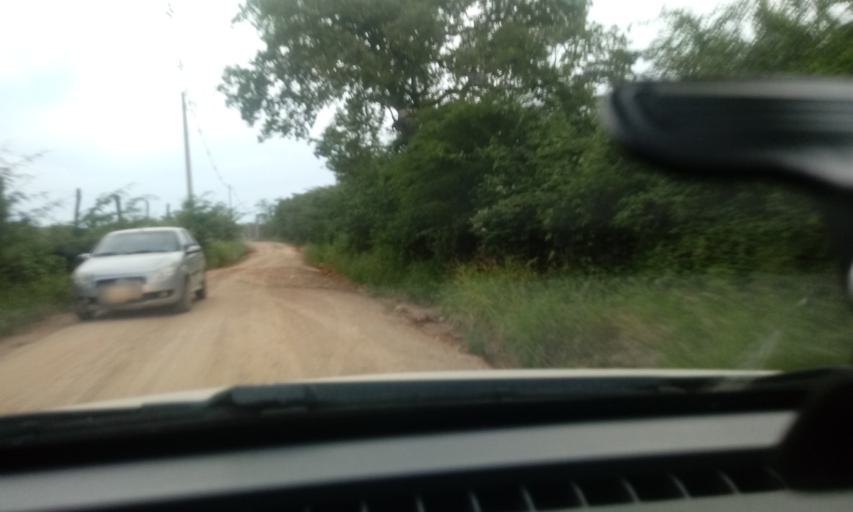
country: BR
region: Bahia
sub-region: Riacho De Santana
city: Riacho de Santana
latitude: -13.8001
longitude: -42.7460
